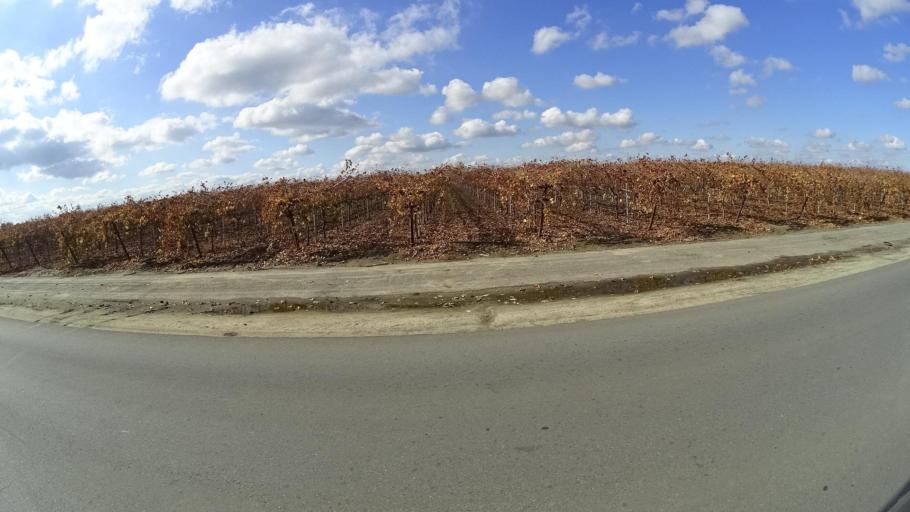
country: US
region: California
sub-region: Kern County
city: McFarland
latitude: 35.6792
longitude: -119.2409
